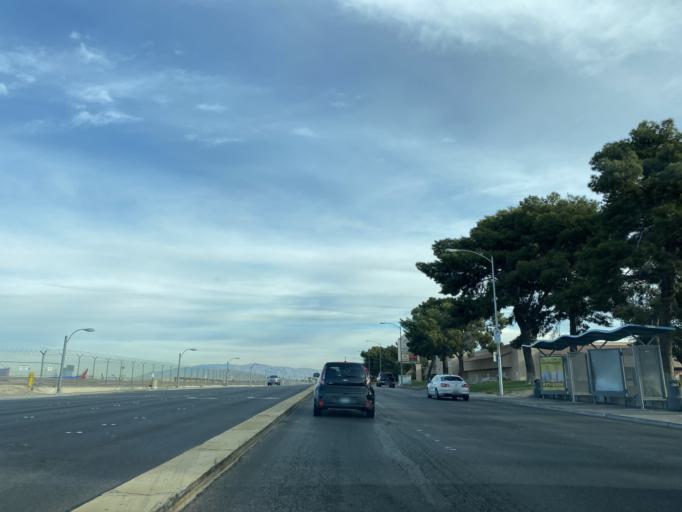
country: US
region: Nevada
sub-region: Clark County
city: Whitney
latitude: 36.0720
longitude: -115.1186
